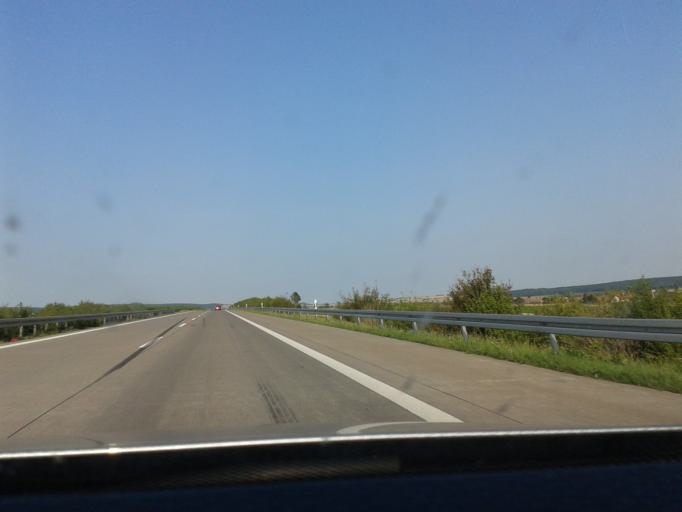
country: DE
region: Saxony-Anhalt
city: Osterhausen
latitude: 51.4420
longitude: 11.4692
